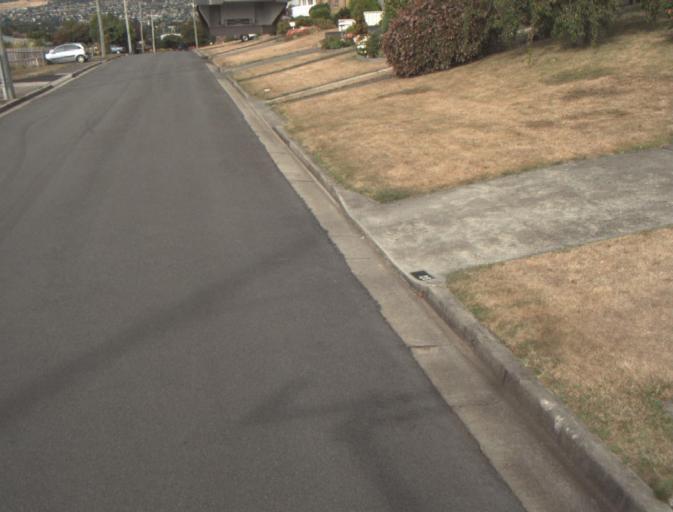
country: AU
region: Tasmania
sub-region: Launceston
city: Invermay
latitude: -41.3914
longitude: 147.1367
